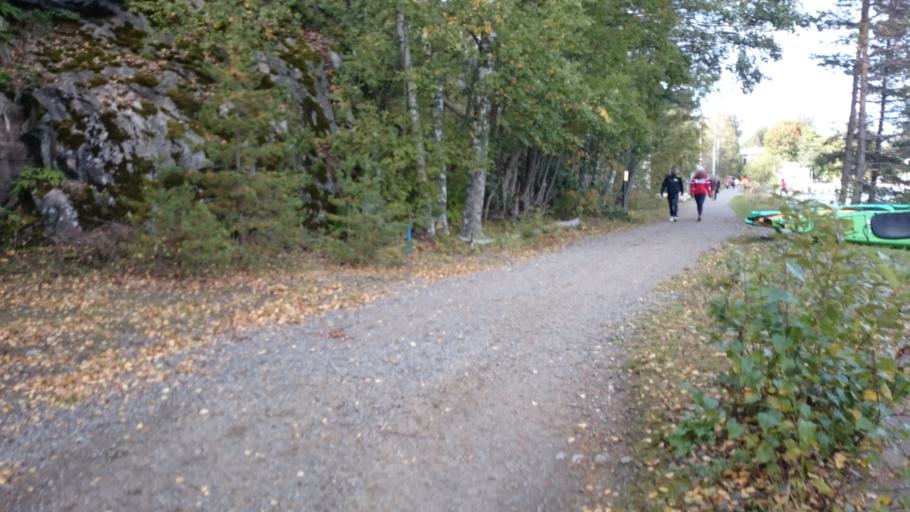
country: FI
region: Uusimaa
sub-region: Helsinki
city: Helsinki
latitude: 60.1356
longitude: 25.0097
